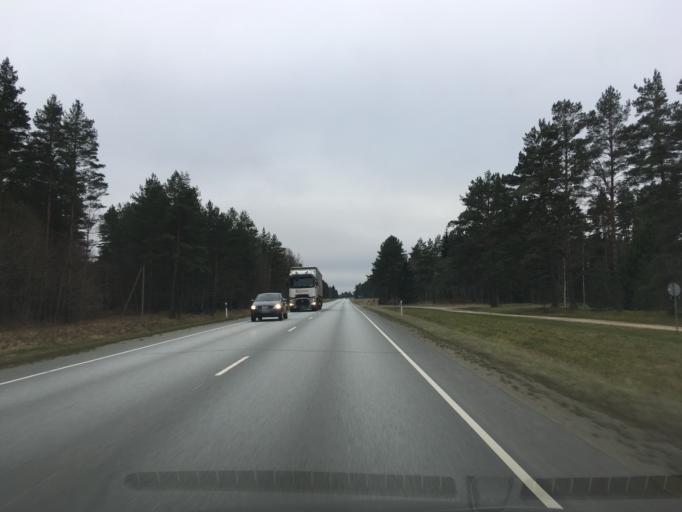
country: EE
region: Laeaene-Virumaa
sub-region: Viru-Nigula vald
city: Kunda
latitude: 59.4027
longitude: 26.6328
